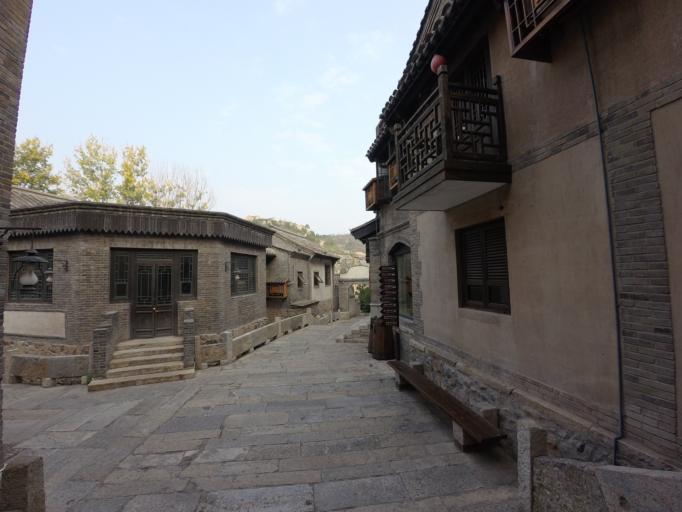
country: CN
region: Beijing
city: Xinchengzi
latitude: 40.6494
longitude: 117.2658
